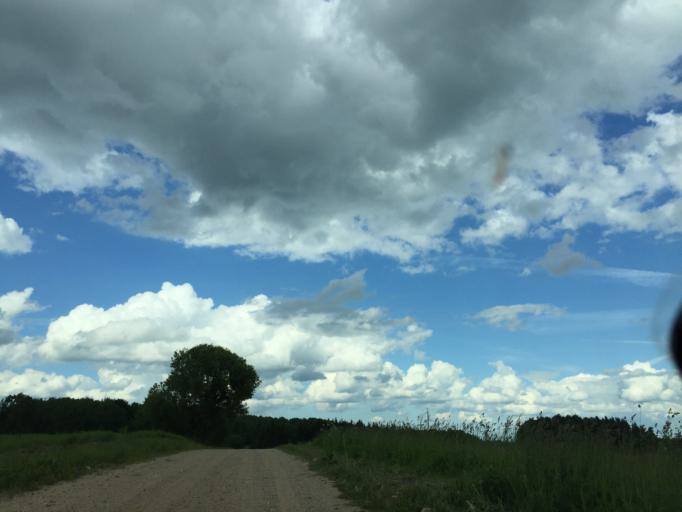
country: LV
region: Dobeles Rajons
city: Dobele
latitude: 56.6510
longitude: 23.2887
